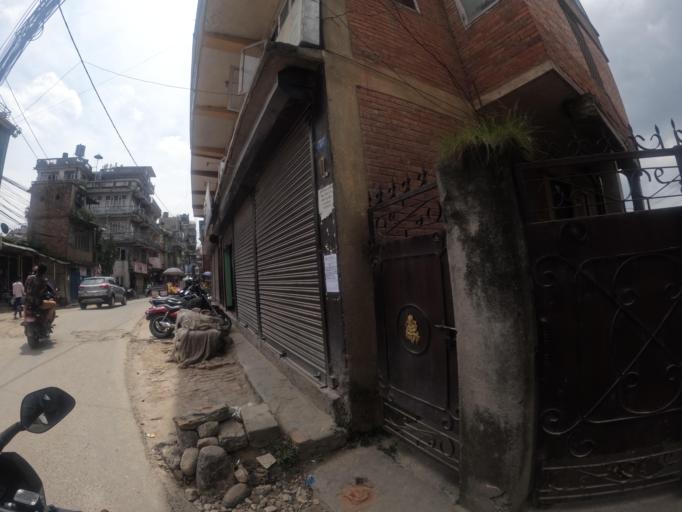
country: NP
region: Central Region
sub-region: Bagmati Zone
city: Bhaktapur
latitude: 27.6839
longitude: 85.3875
